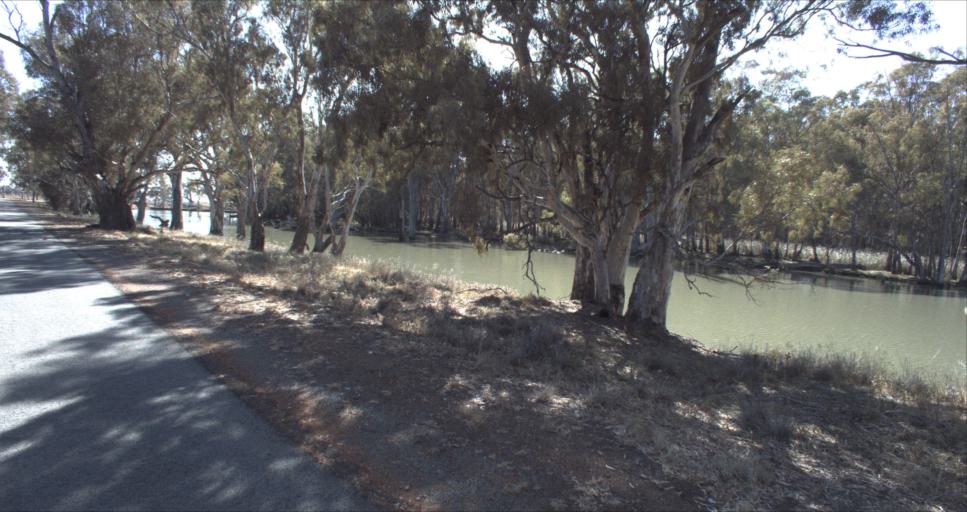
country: AU
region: New South Wales
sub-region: Leeton
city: Leeton
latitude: -34.6069
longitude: 146.2632
